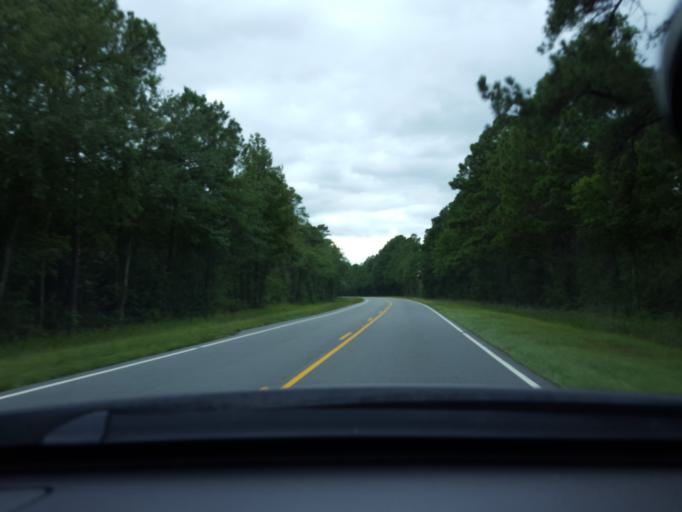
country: US
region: North Carolina
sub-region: Bladen County
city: Elizabethtown
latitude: 34.7050
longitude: -78.4704
